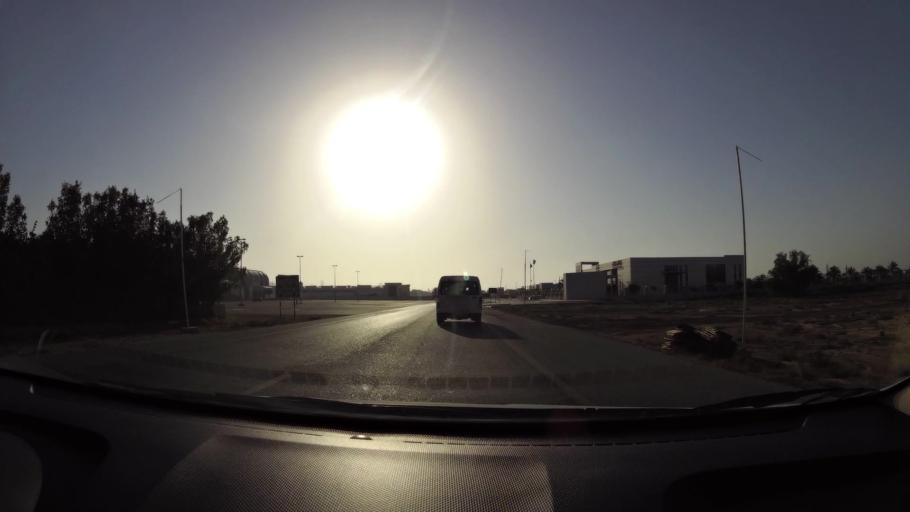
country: AE
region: Ajman
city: Ajman
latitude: 25.4034
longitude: 55.4882
